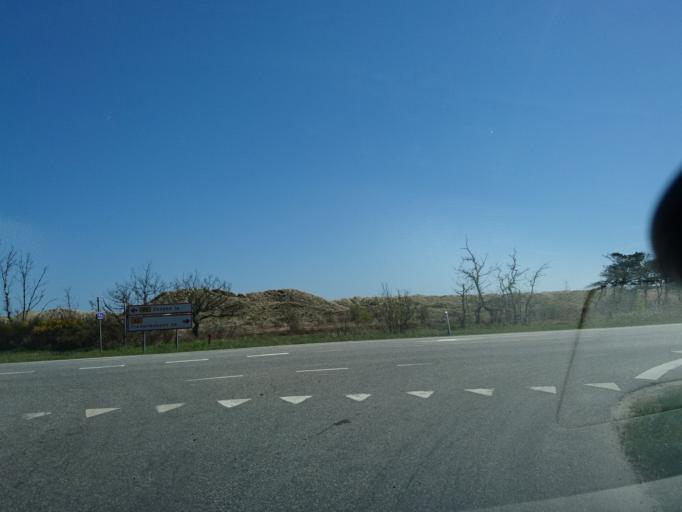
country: DK
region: North Denmark
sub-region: Frederikshavn Kommune
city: Strandby
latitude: 57.6300
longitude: 10.4481
